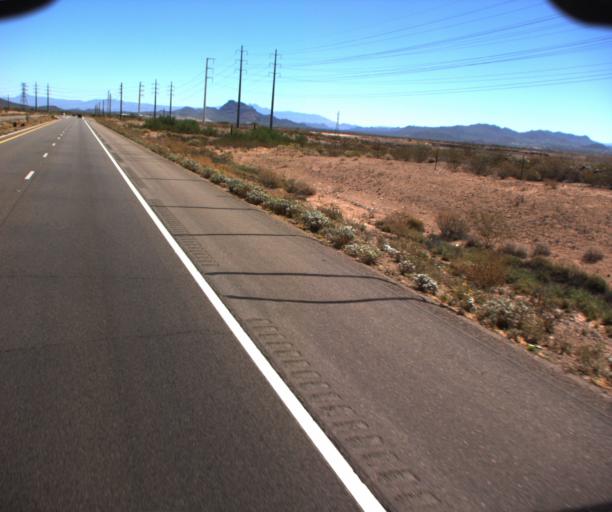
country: US
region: Arizona
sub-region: Maricopa County
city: Mesa
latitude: 33.4933
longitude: -111.8083
